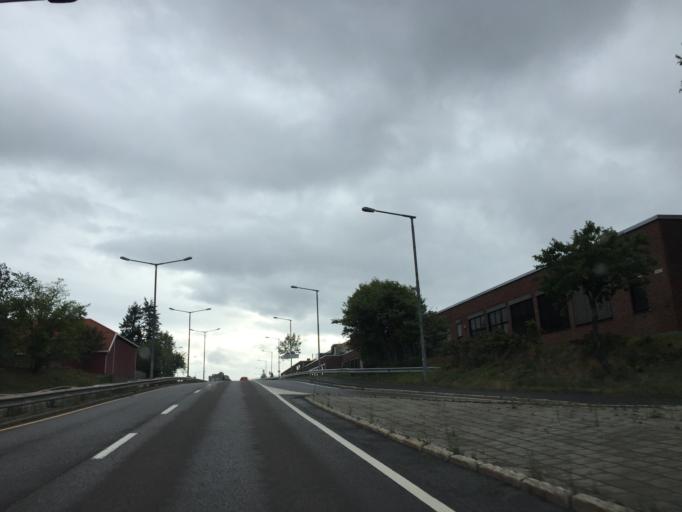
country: NO
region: Oslo
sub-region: Oslo
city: Oslo
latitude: 59.9328
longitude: 10.8277
